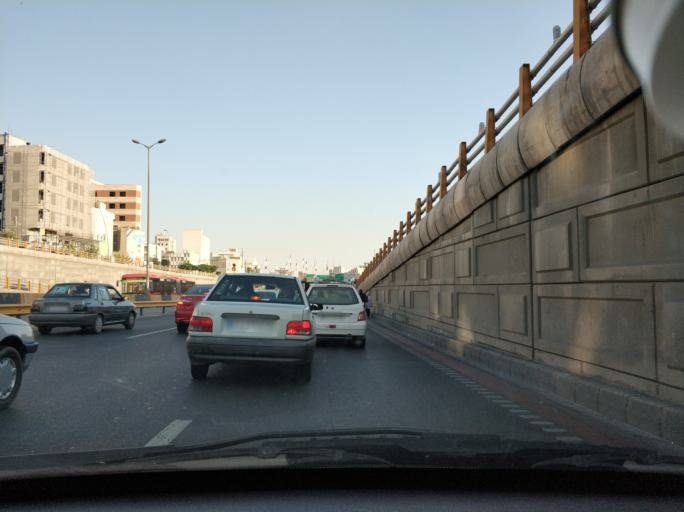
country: IR
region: Tehran
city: Tehran
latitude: 35.6921
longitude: 51.4568
